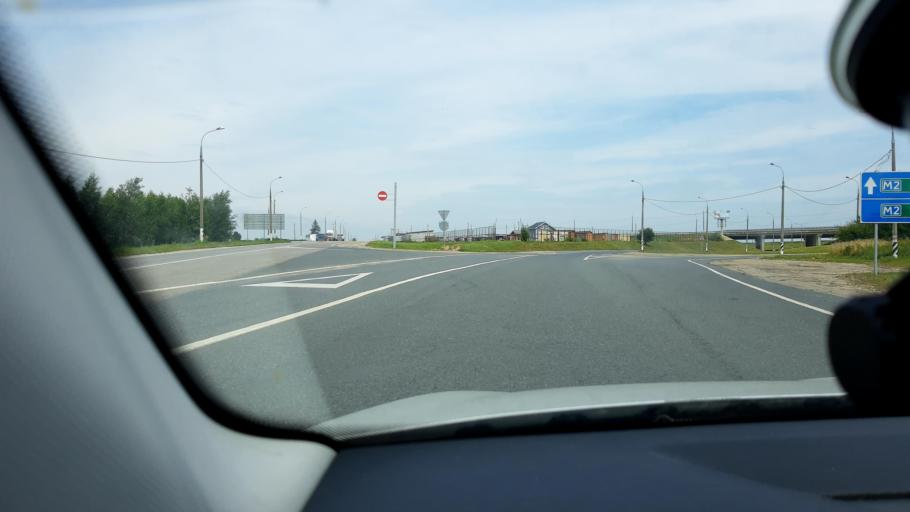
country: RU
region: Moskovskaya
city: Serpukhov
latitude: 54.8311
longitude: 37.4581
